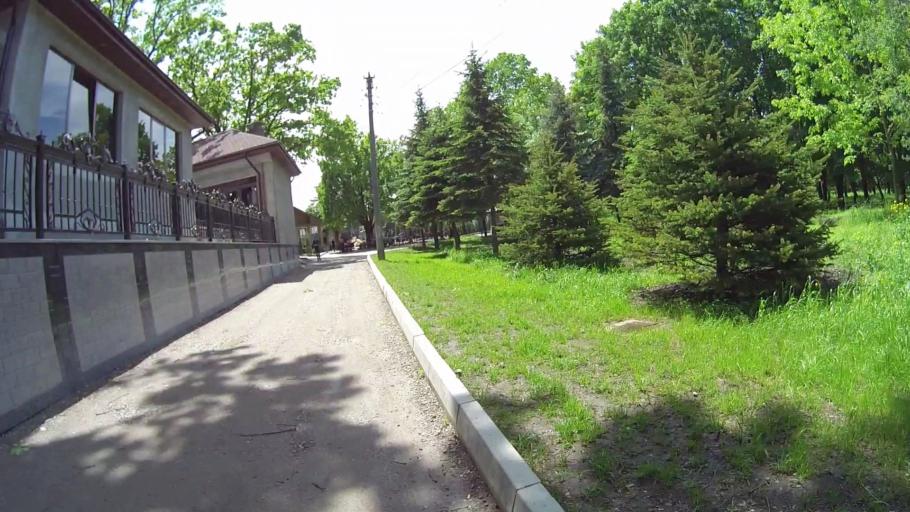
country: RU
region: Kabardino-Balkariya
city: Vol'nyy Aul
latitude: 43.4598
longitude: 43.5884
